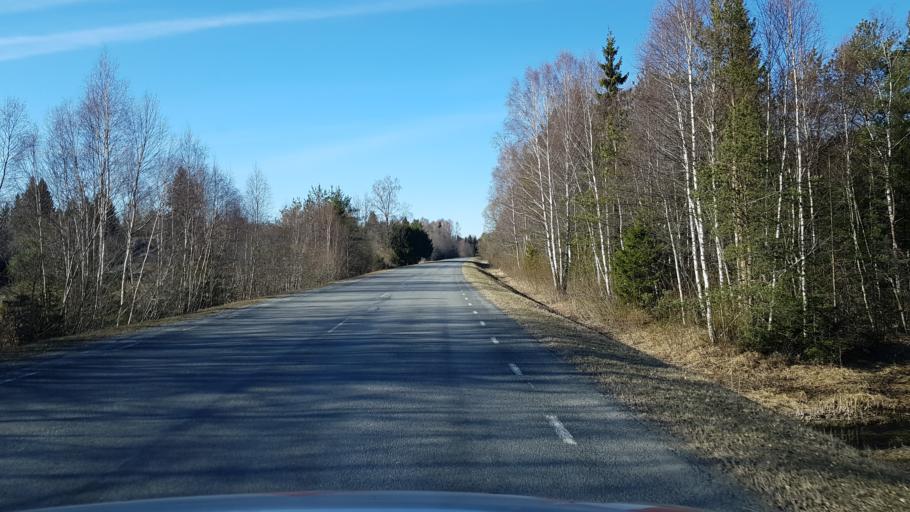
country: EE
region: Harju
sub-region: Keila linn
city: Keila
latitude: 59.2434
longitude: 24.4620
